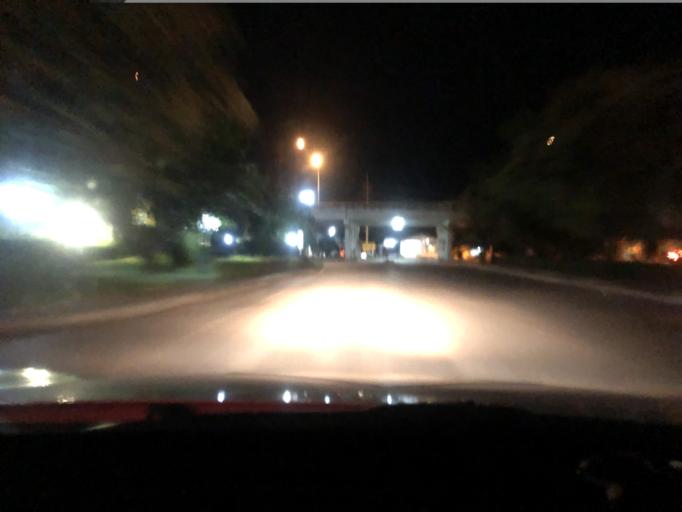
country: TH
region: Nakhon Sawan
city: Takhli
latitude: 15.2639
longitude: 100.3471
